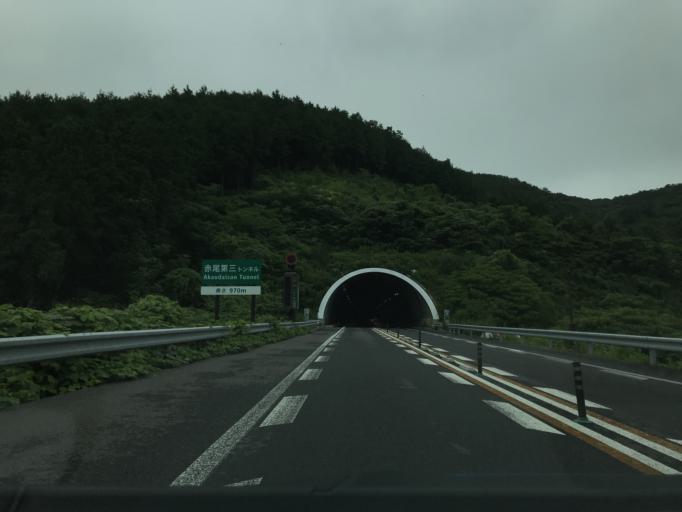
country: JP
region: Fukuoka
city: Nakatsu
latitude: 33.5120
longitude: 131.2841
